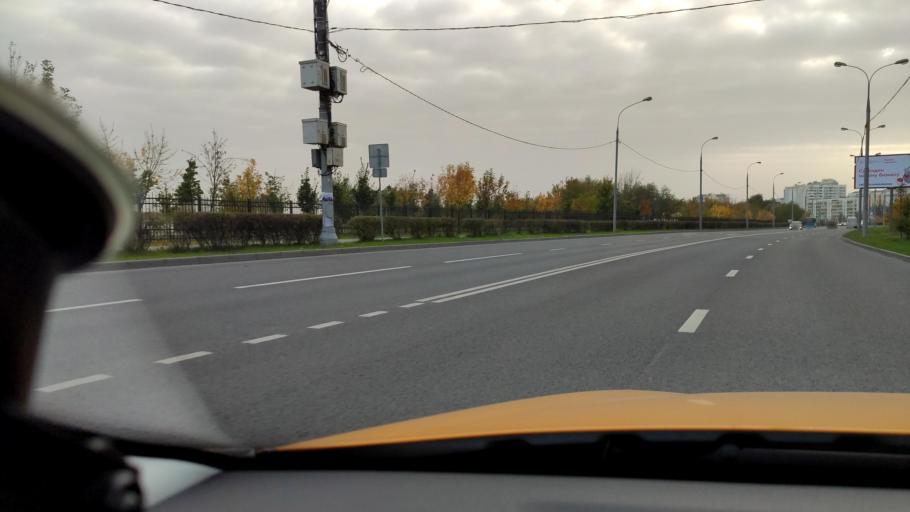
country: RU
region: Moscow
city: Kapotnya
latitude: 55.6662
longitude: 37.7903
